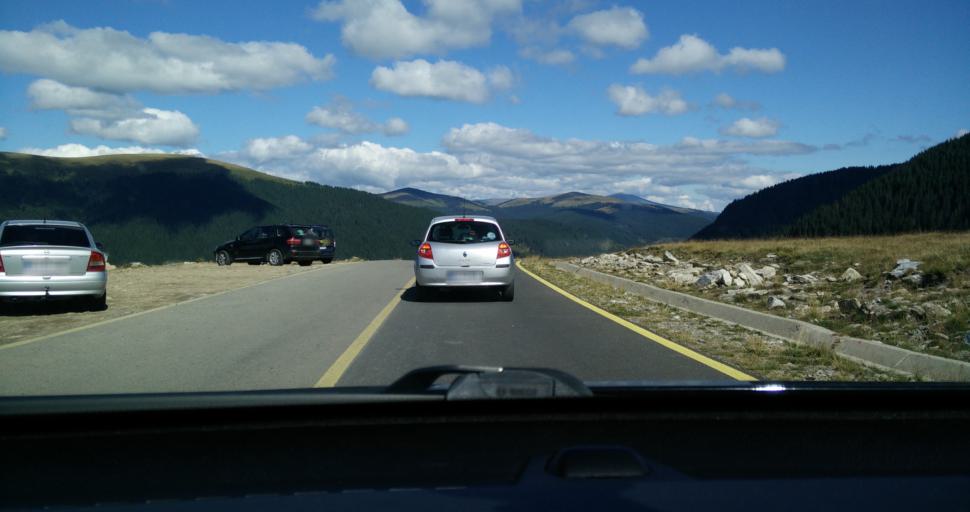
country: RO
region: Gorj
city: Novaci-Straini
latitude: 45.3850
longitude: 23.6425
